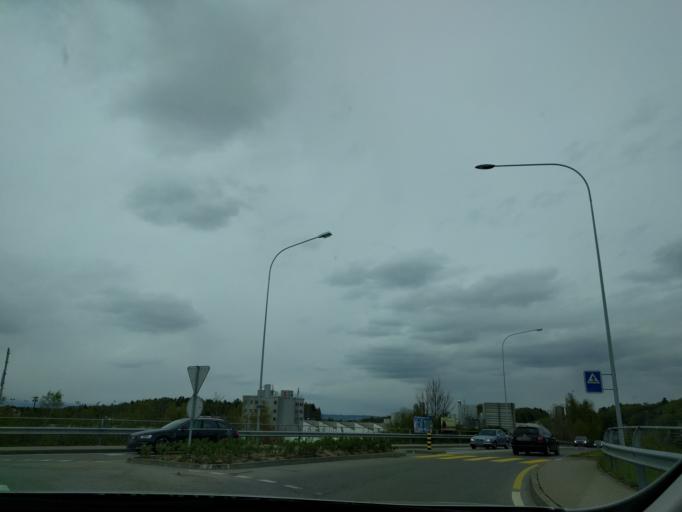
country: CH
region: Fribourg
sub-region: Sense District
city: Dudingen
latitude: 46.8533
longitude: 7.1929
